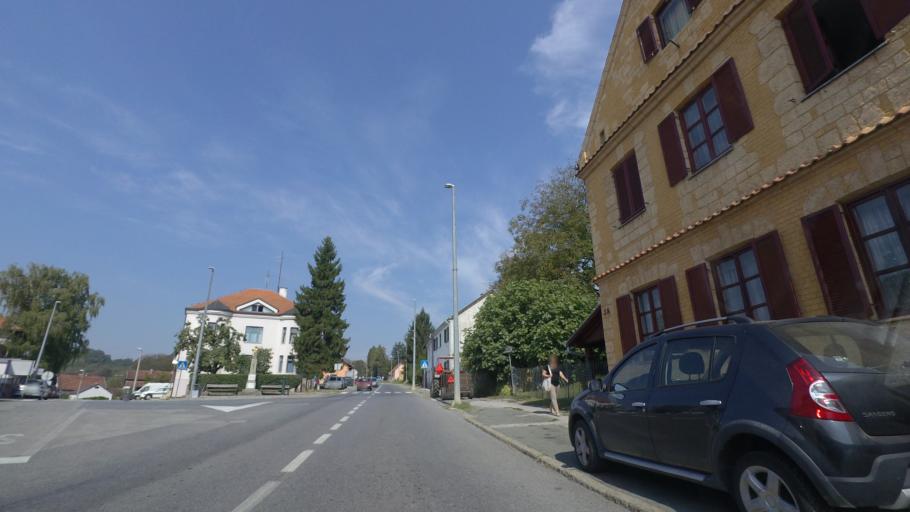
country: HR
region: Sisacko-Moslavacka
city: Hrvatska Kostajnica
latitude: 45.2291
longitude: 16.5361
